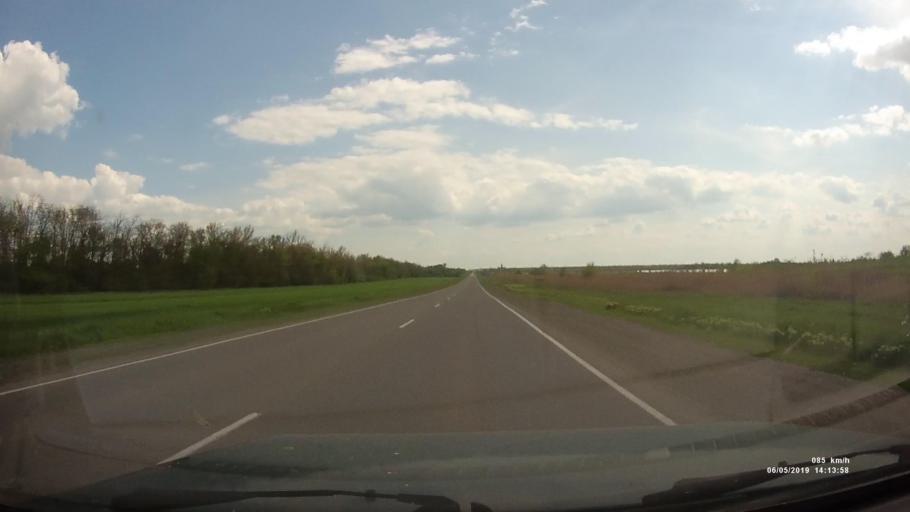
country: RU
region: Rostov
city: Kamenolomni
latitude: 47.6540
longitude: 40.2948
